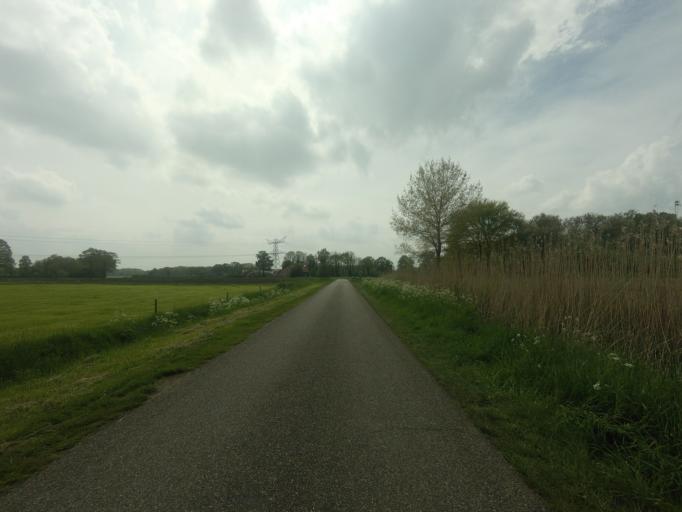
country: NL
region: Overijssel
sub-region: Gemeente Hof van Twente
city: Delden
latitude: 52.2470
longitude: 6.6819
